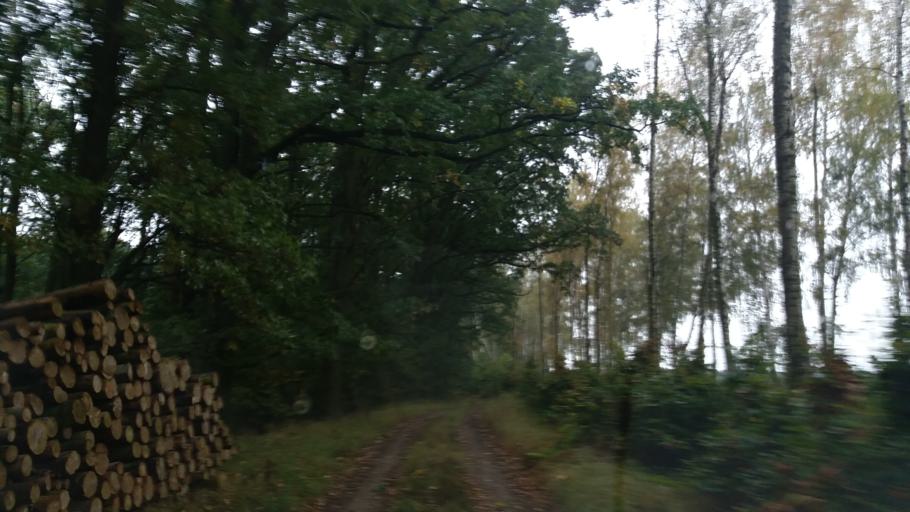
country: PL
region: West Pomeranian Voivodeship
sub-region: Powiat choszczenski
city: Pelczyce
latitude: 53.0698
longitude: 15.2744
